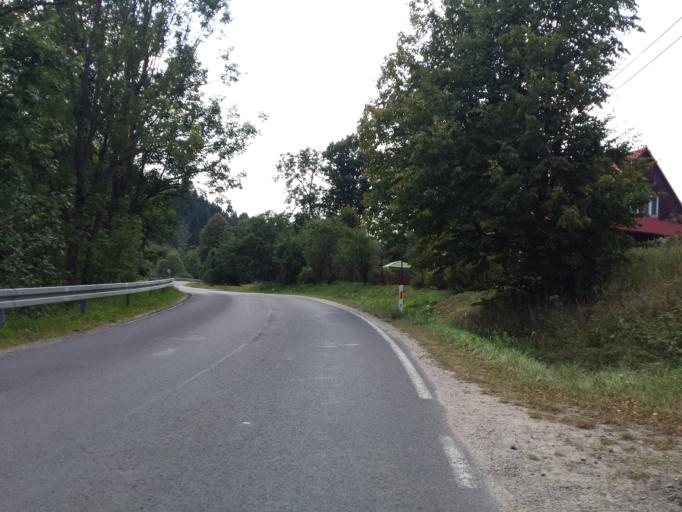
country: PL
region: Subcarpathian Voivodeship
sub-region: Powiat leski
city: Cisna
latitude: 49.2221
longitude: 22.3432
